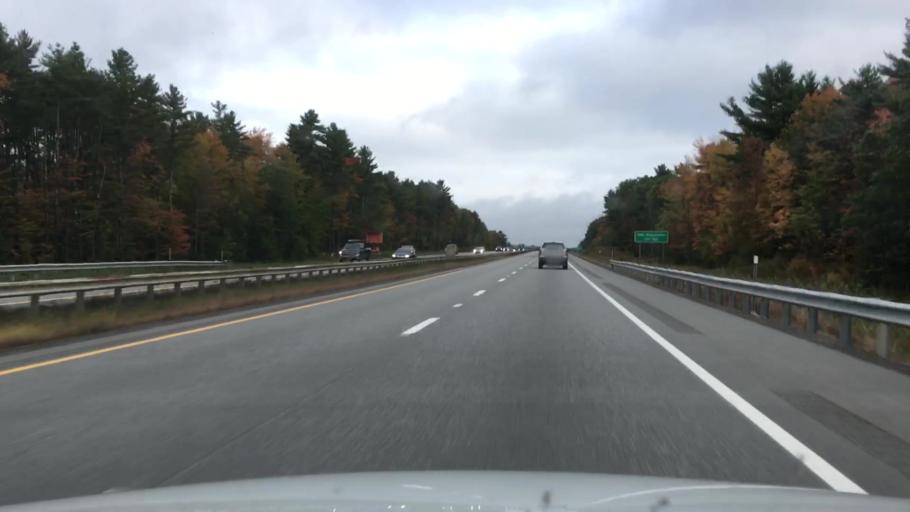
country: US
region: Maine
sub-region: Cumberland County
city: Cumberland Center
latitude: 43.8714
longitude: -70.3288
